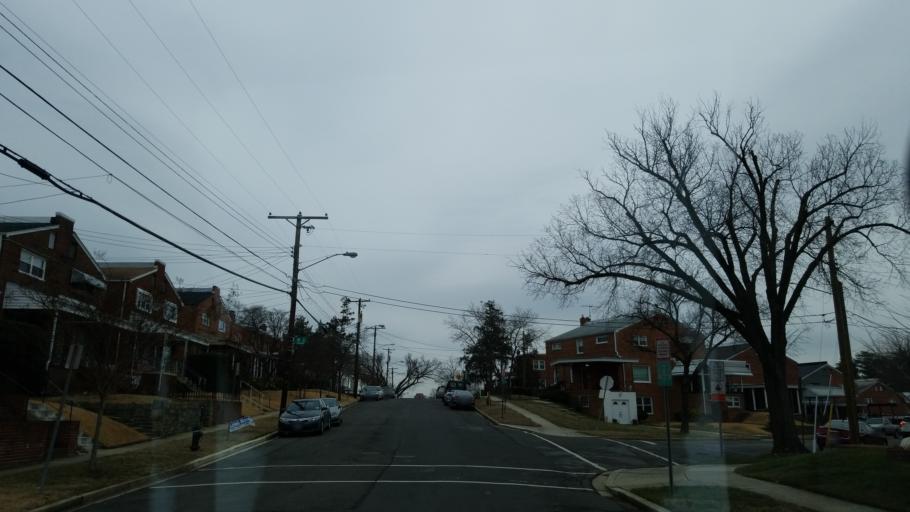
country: US
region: Maryland
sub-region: Prince George's County
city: Chillum
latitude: 38.9545
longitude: -76.9949
